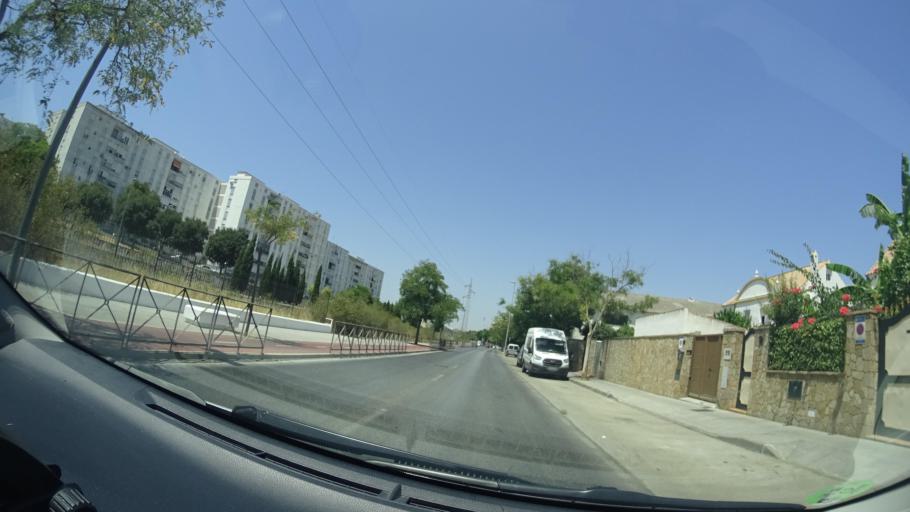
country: ES
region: Andalusia
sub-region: Provincia de Cadiz
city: Jerez de la Frontera
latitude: 36.6745
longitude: -6.1228
